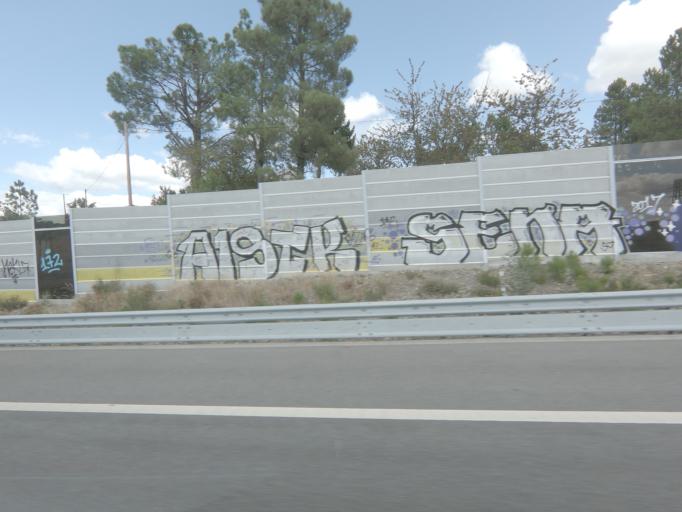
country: PT
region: Vila Real
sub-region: Santa Marta de Penaguiao
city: Santa Marta de Penaguiao
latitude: 41.2773
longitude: -7.8578
